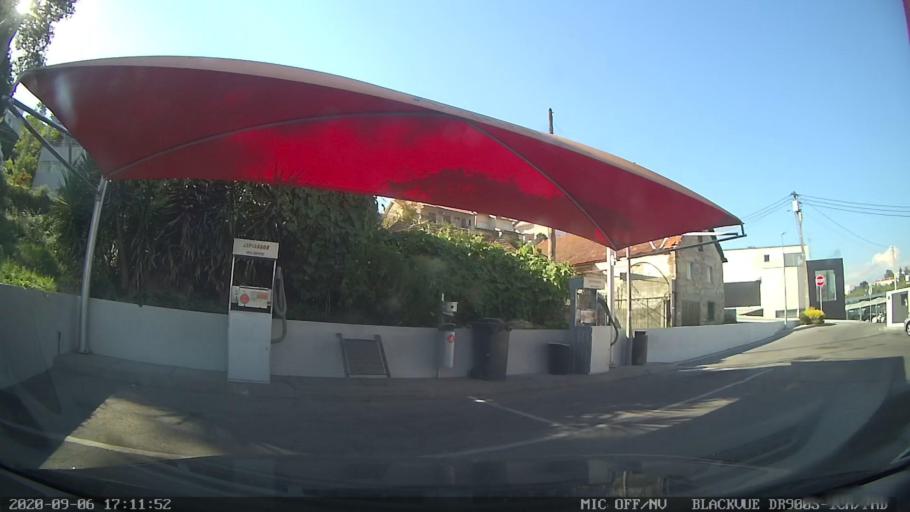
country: PT
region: Porto
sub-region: Amarante
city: Amarante
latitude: 41.2731
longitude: -8.0902
